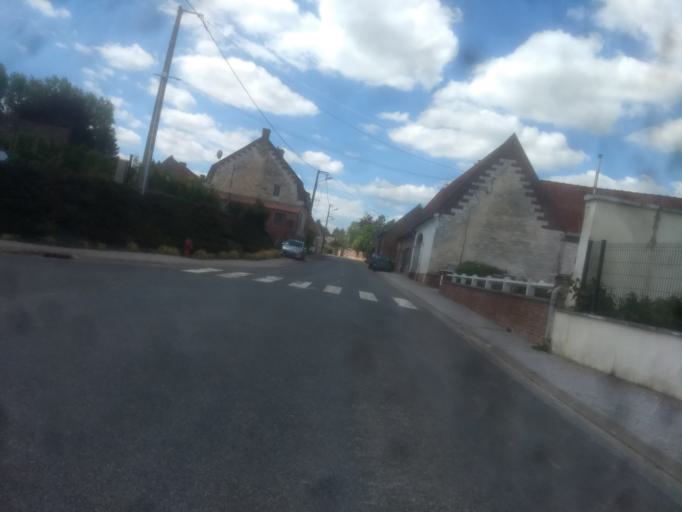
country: FR
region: Nord-Pas-de-Calais
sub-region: Departement du Pas-de-Calais
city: Riviere
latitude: 50.2304
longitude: 2.6782
